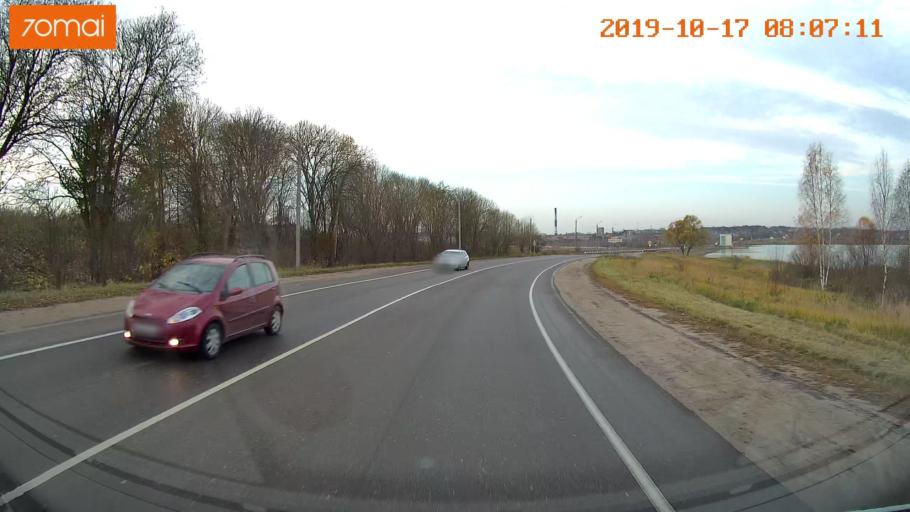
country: RU
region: Vladimir
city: Kol'chugino
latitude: 56.3168
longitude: 39.4028
